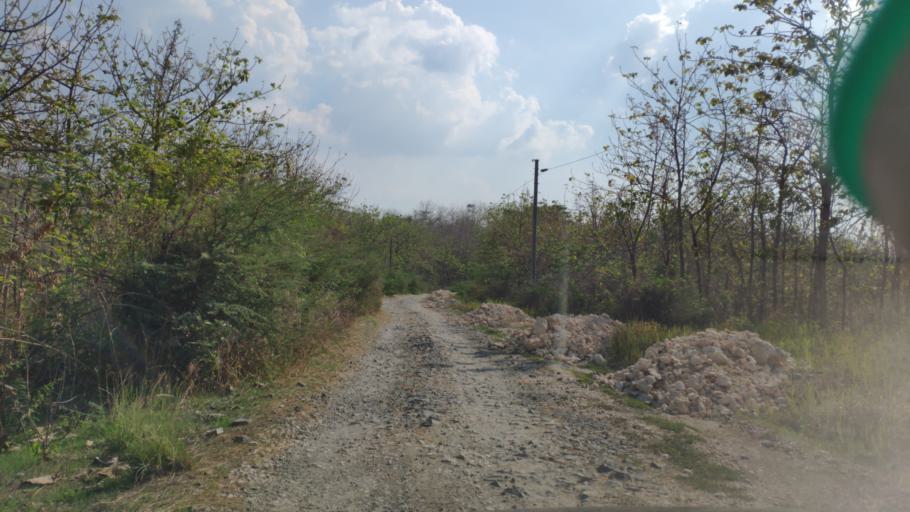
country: ID
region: Central Java
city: Randublatung
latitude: -7.2229
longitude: 111.3473
